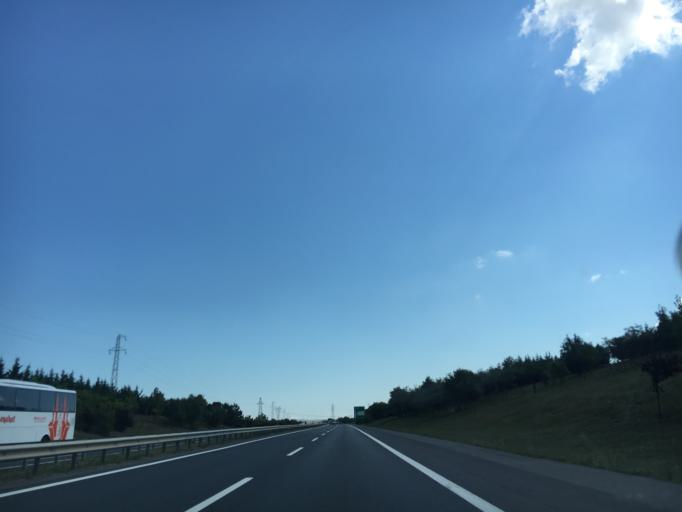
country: TR
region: Istanbul
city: Canta
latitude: 41.0848
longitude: 28.1353
